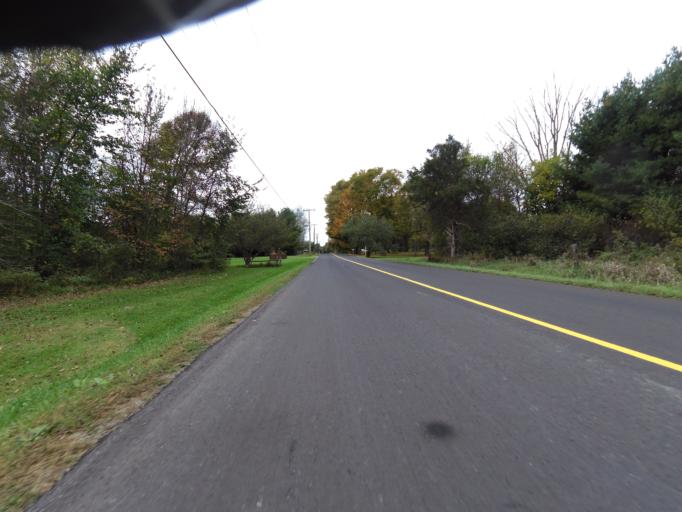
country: CA
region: Ontario
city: Gananoque
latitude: 44.5822
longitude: -76.0689
